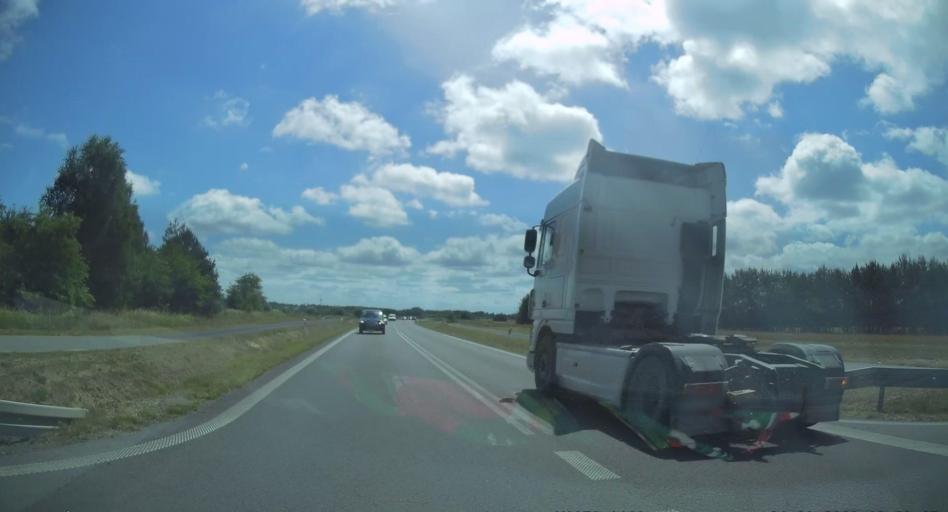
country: PL
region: Subcarpathian Voivodeship
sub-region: Powiat mielecki
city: Padew Narodowa
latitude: 50.3773
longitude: 21.4756
